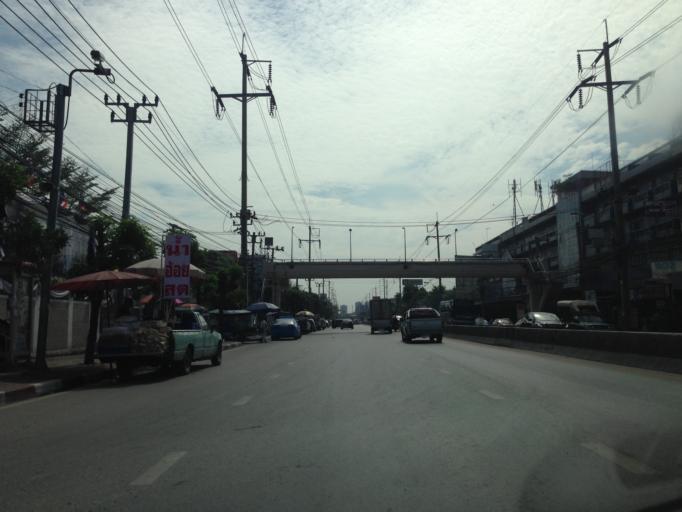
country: TH
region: Phra Nakhon Si Ayutthaya
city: Ban Bang Kadi Pathum Thani
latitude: 13.9487
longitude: 100.5464
